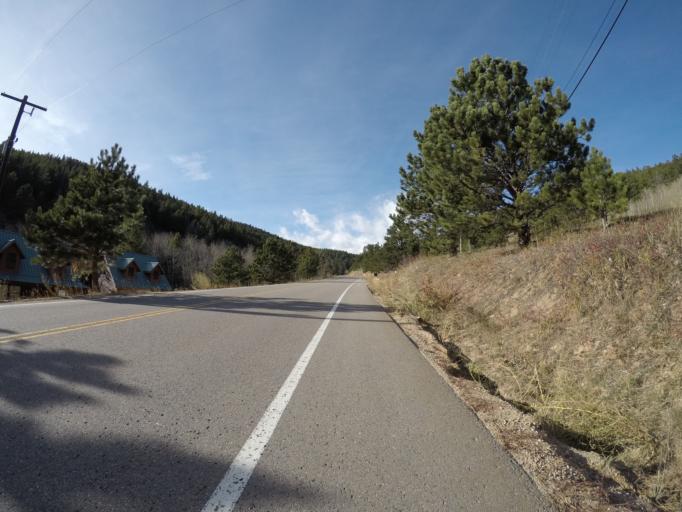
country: US
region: Colorado
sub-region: Boulder County
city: Nederland
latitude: 40.0638
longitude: -105.5002
